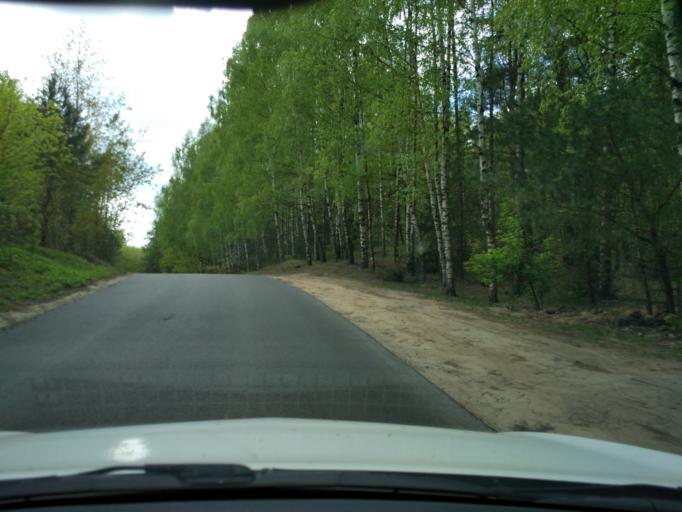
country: LT
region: Vilnius County
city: Rasos
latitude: 54.6944
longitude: 25.3351
